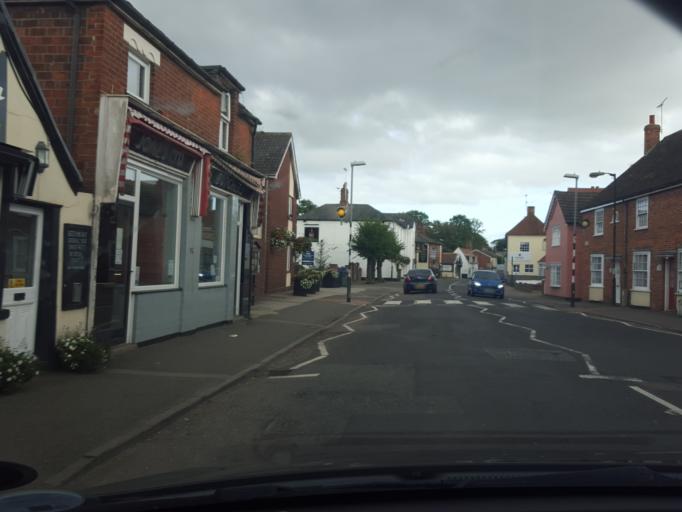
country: GB
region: England
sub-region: Essex
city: Little Clacton
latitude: 51.8576
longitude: 1.1624
